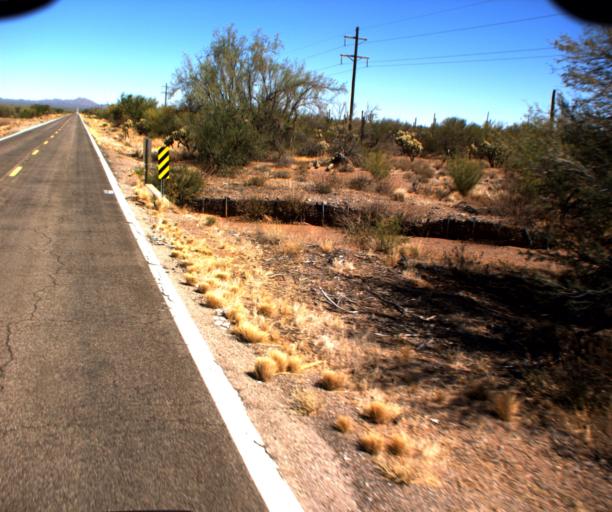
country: US
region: Arizona
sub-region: Pima County
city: Sells
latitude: 32.0631
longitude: -112.0358
